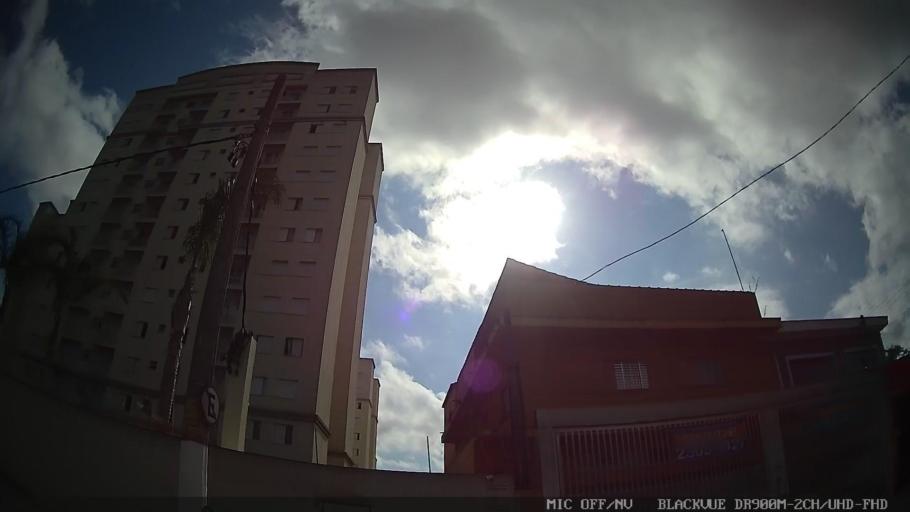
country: BR
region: Sao Paulo
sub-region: Guarulhos
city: Guarulhos
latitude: -23.5120
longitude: -46.4771
